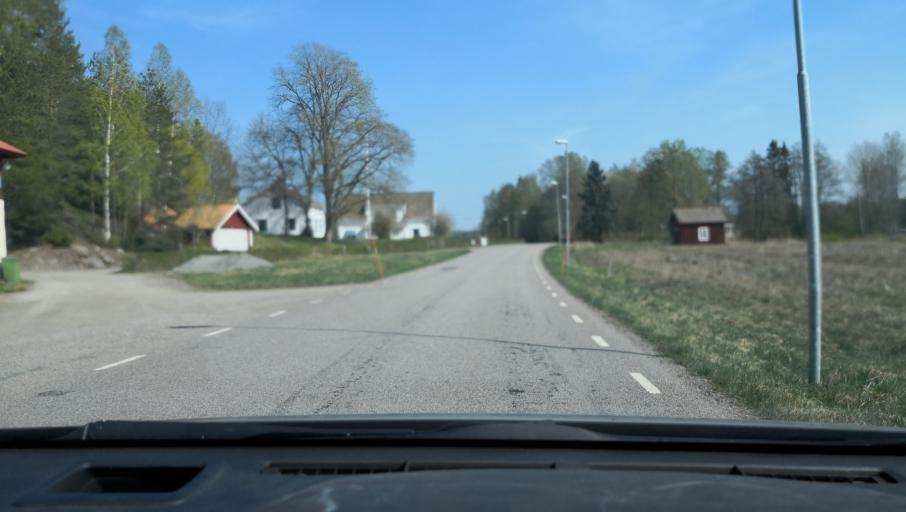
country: SE
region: Uppsala
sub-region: Heby Kommun
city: Heby
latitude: 60.0351
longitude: 16.7930
